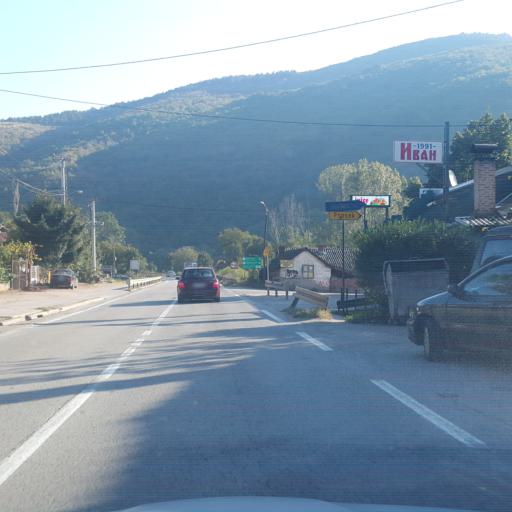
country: RS
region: Central Serbia
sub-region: Nisavski Okrug
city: Niska Banja
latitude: 43.3125
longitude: 22.0509
